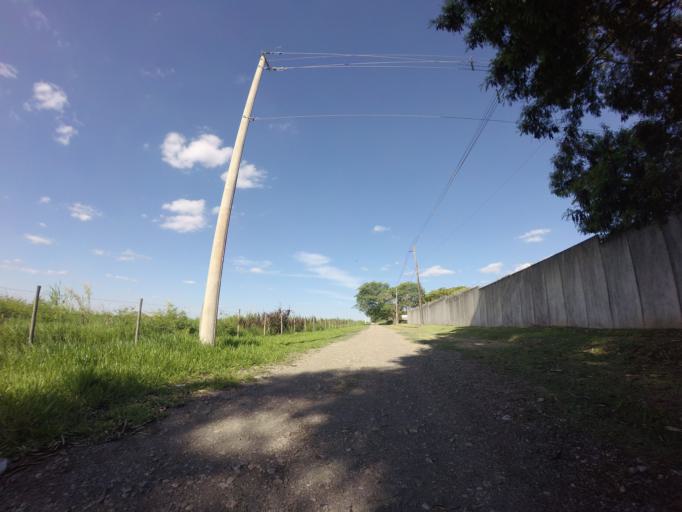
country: BR
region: Sao Paulo
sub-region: Piracicaba
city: Piracicaba
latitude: -22.7497
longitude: -47.5908
